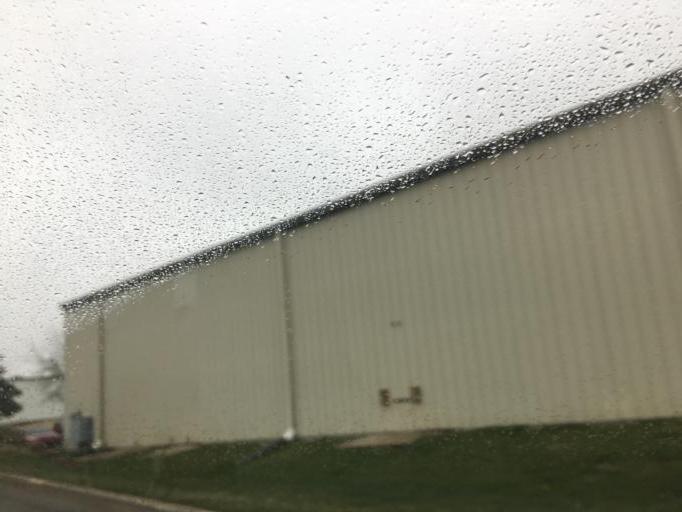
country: US
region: Kansas
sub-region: Johnson County
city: Olathe
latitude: 38.8890
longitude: -94.7972
